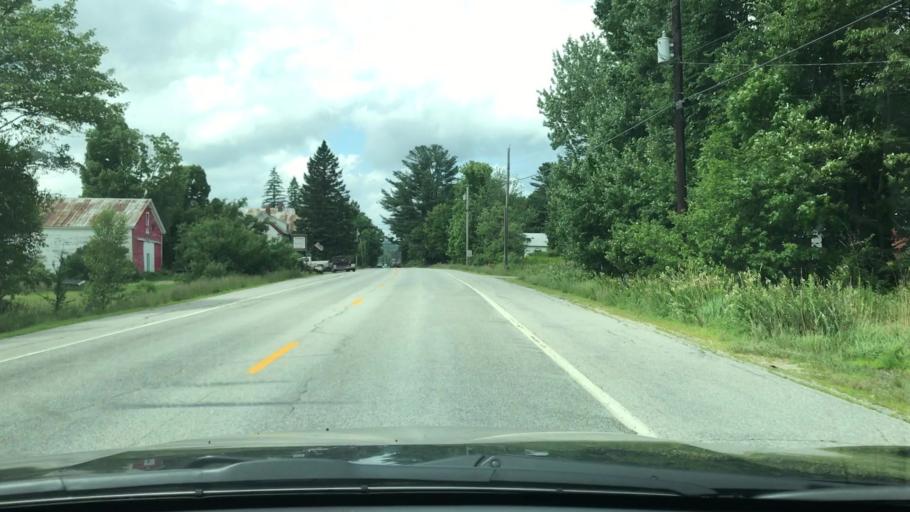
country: US
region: Maine
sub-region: Oxford County
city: West Paris
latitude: 44.3740
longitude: -70.6082
